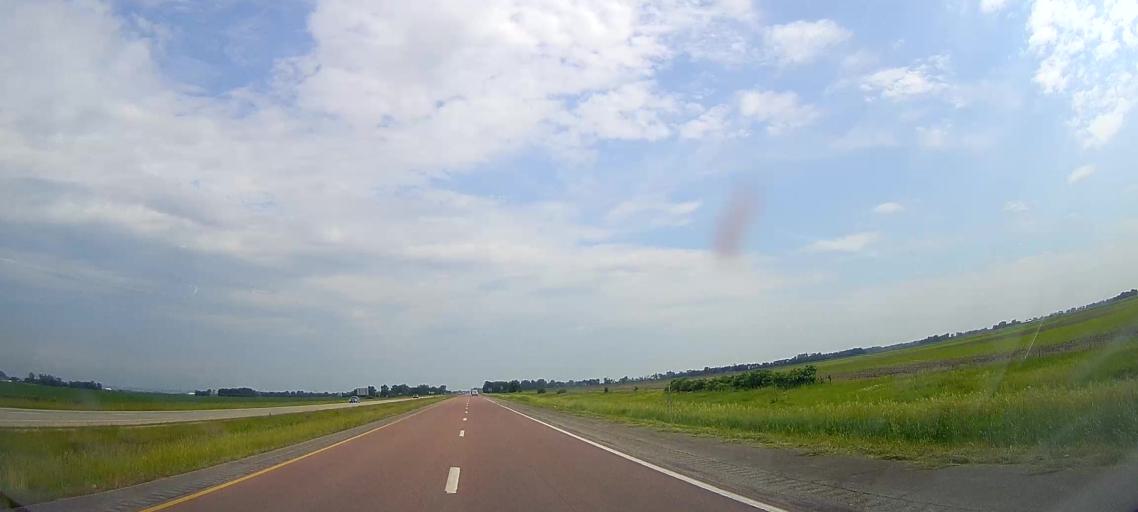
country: US
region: Iowa
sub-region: Monona County
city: Onawa
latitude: 42.0061
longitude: -96.1168
